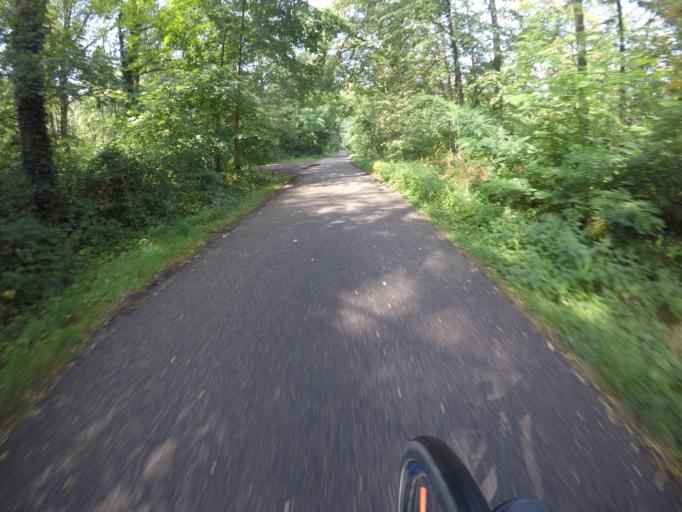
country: DE
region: Baden-Wuerttemberg
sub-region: Karlsruhe Region
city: Ketsch
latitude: 49.3627
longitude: 8.5562
